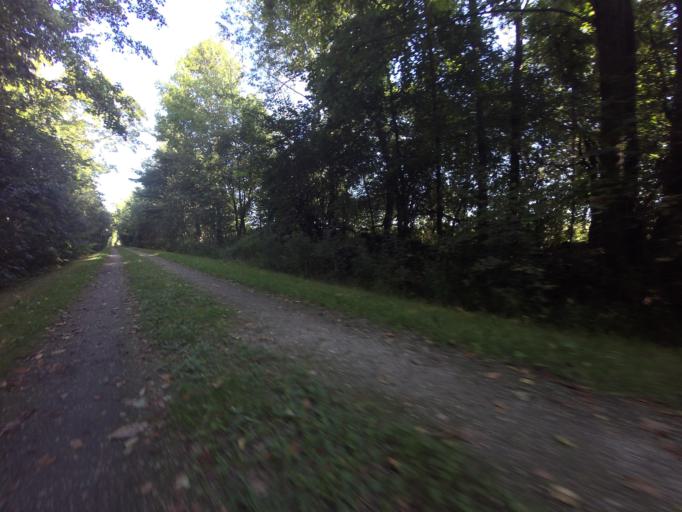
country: CA
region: Ontario
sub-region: Wellington County
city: Guelph
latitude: 43.6565
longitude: -80.4238
